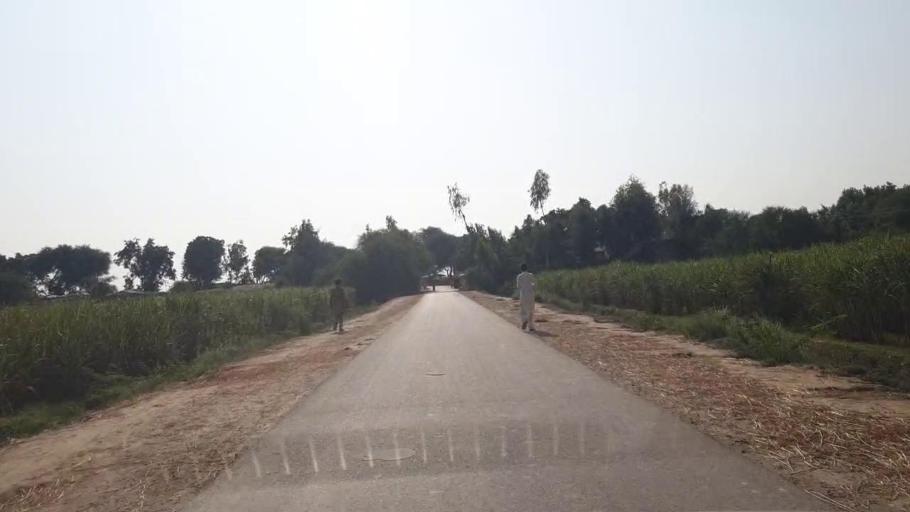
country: PK
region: Sindh
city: Matli
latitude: 24.9841
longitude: 68.6608
